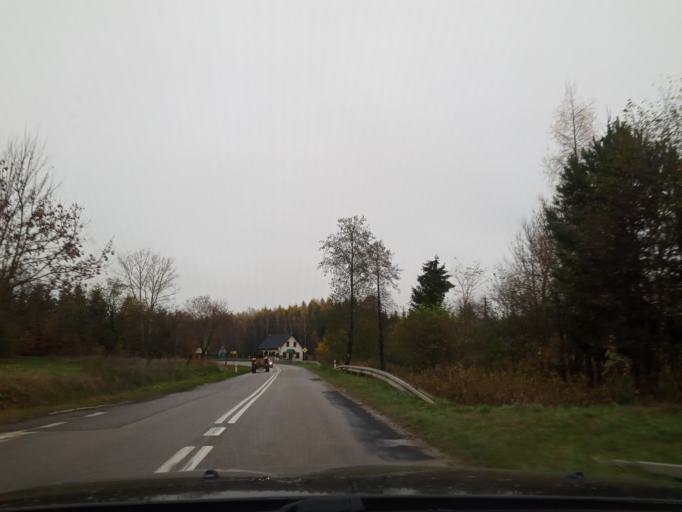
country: PL
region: Swietokrzyskie
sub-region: Powiat pinczowski
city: Dzialoszyce
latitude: 50.4270
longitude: 20.3439
